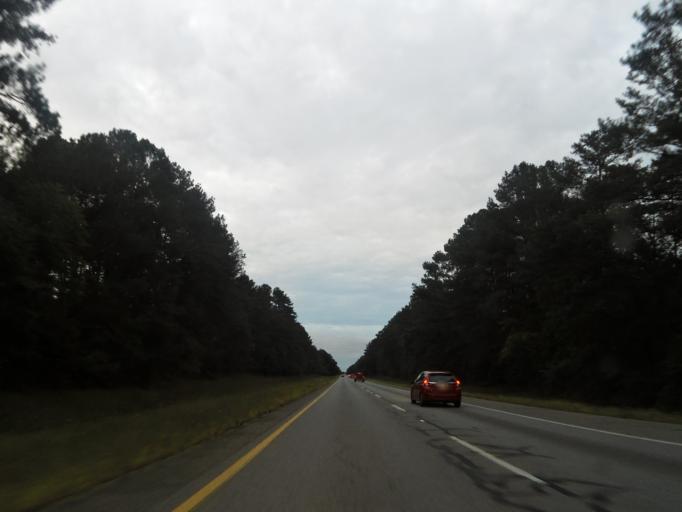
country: US
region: Alabama
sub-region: Saint Clair County
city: Ashville
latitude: 33.8740
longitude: -86.2677
